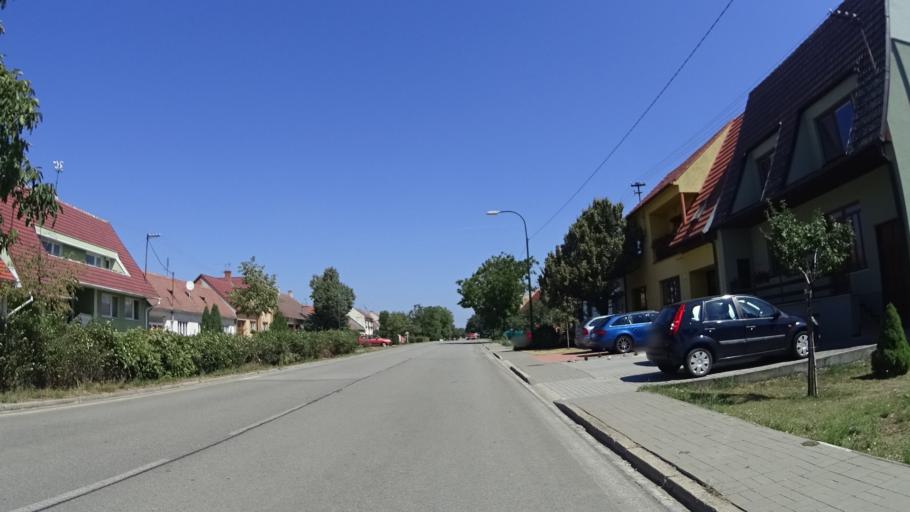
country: CZ
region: South Moravian
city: Sudomerice
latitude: 48.8653
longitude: 17.2549
